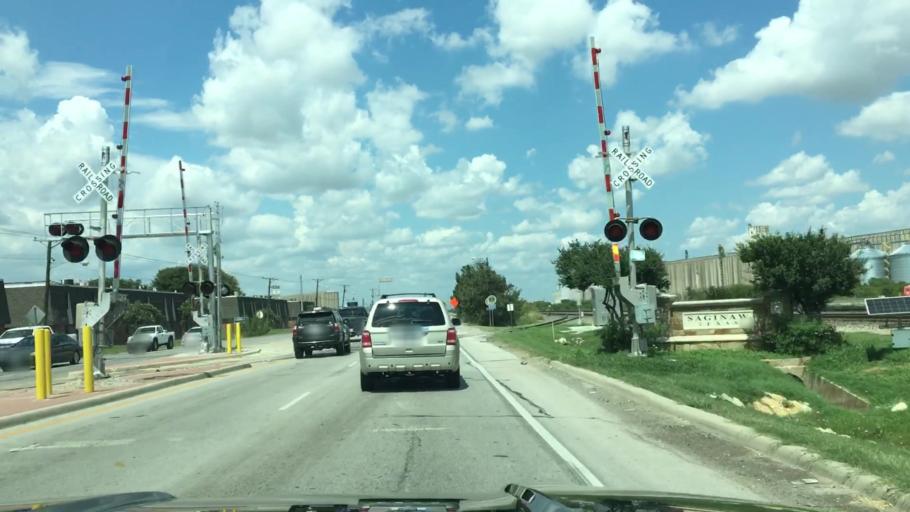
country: US
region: Texas
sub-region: Tarrant County
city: Saginaw
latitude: 32.8481
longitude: -97.3600
